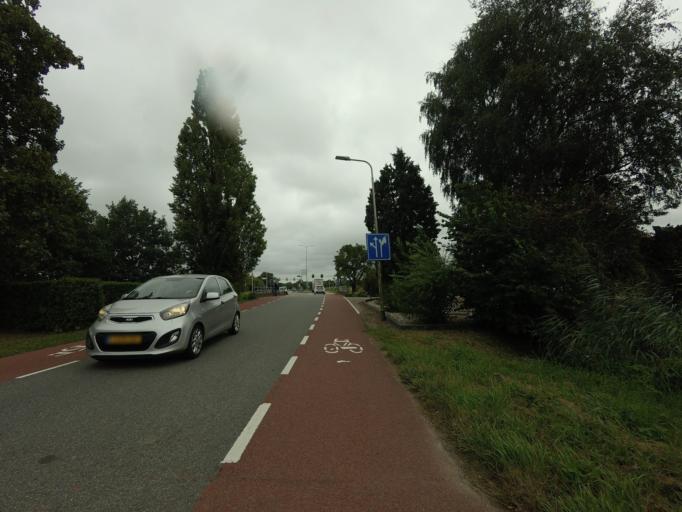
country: NL
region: Gelderland
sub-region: Gemeente Overbetuwe
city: Driel
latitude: 51.9485
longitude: 5.8285
